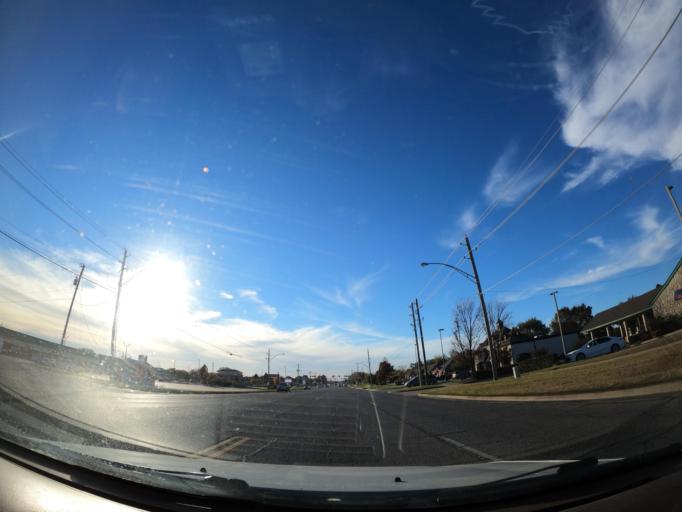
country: US
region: Oklahoma
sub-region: Tulsa County
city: Owasso
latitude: 36.2786
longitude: -95.8344
